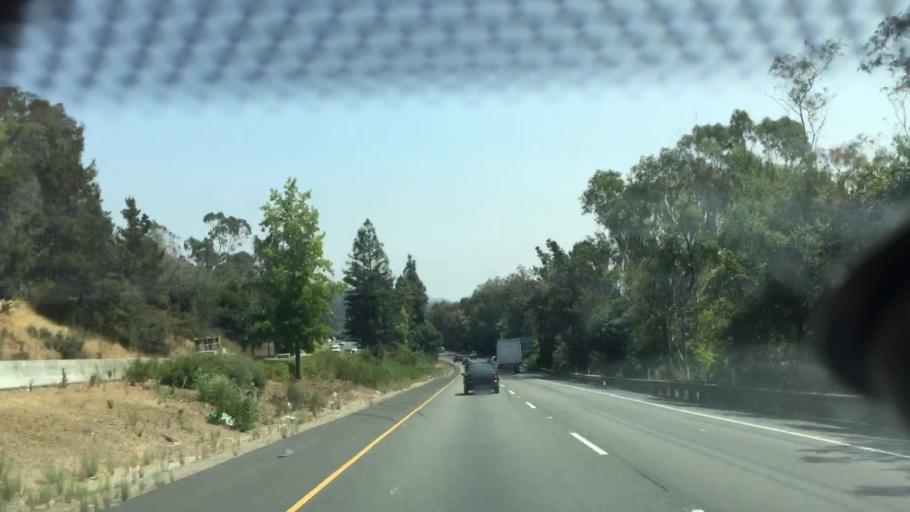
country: US
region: California
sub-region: Alameda County
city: Piedmont
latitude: 37.8045
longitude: -122.1915
